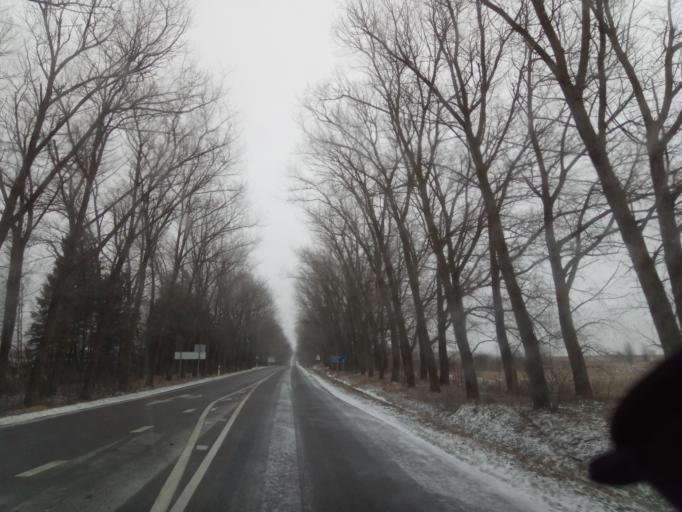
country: LT
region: Utenos apskritis
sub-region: Anyksciai
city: Anyksciai
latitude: 55.3942
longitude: 25.0757
